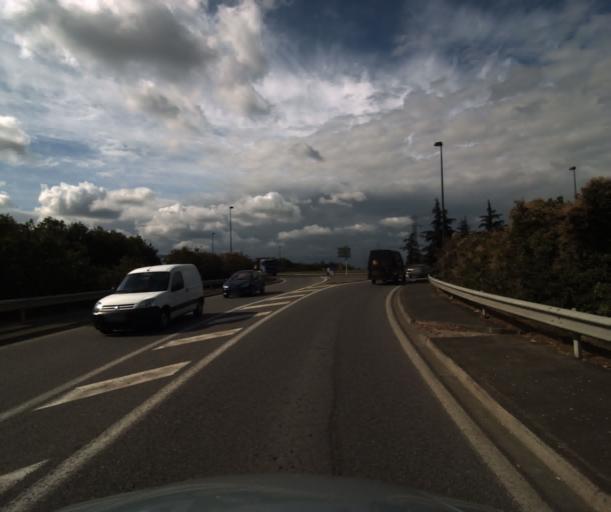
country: FR
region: Midi-Pyrenees
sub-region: Departement de la Haute-Garonne
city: Seysses
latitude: 43.4773
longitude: 1.3193
